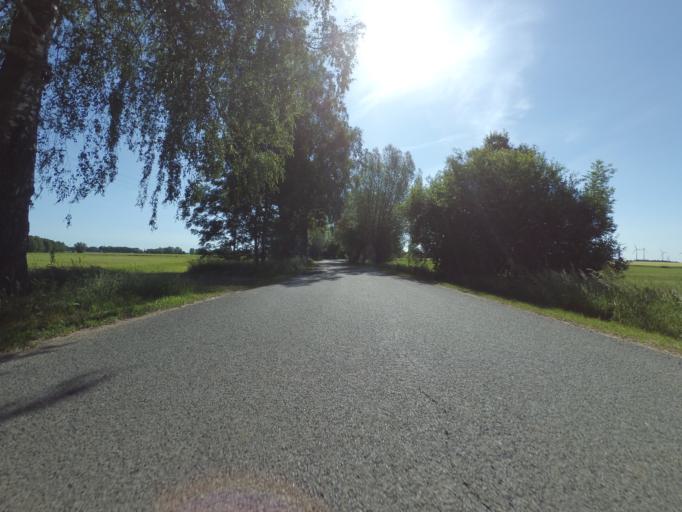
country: DE
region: Brandenburg
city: Triglitz
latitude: 53.2668
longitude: 12.1081
